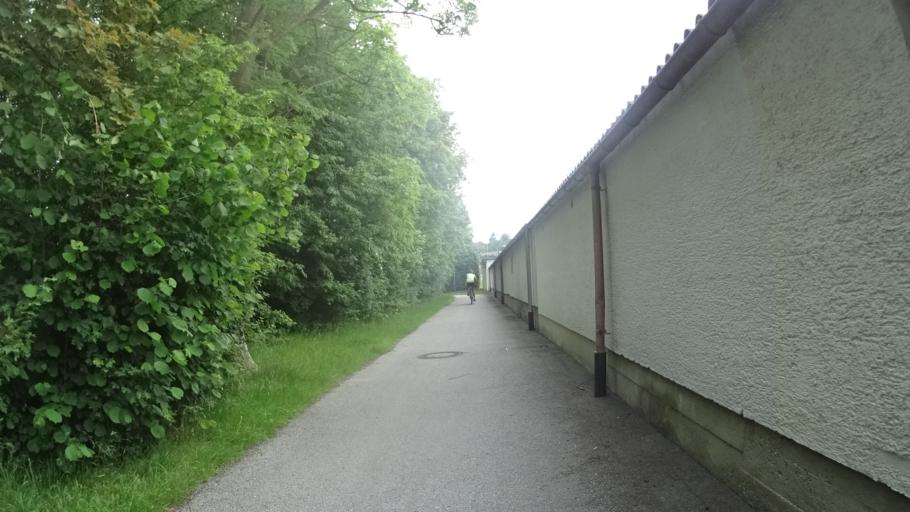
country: DE
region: Bavaria
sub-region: Lower Bavaria
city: Passau
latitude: 48.5553
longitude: 13.4346
